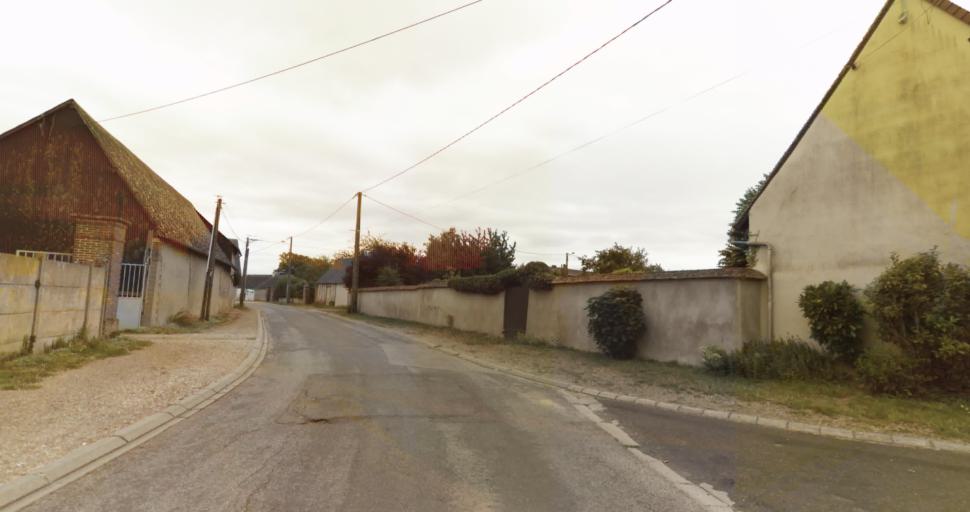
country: FR
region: Haute-Normandie
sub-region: Departement de l'Eure
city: Pacy-sur-Eure
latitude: 48.9500
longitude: 1.3038
